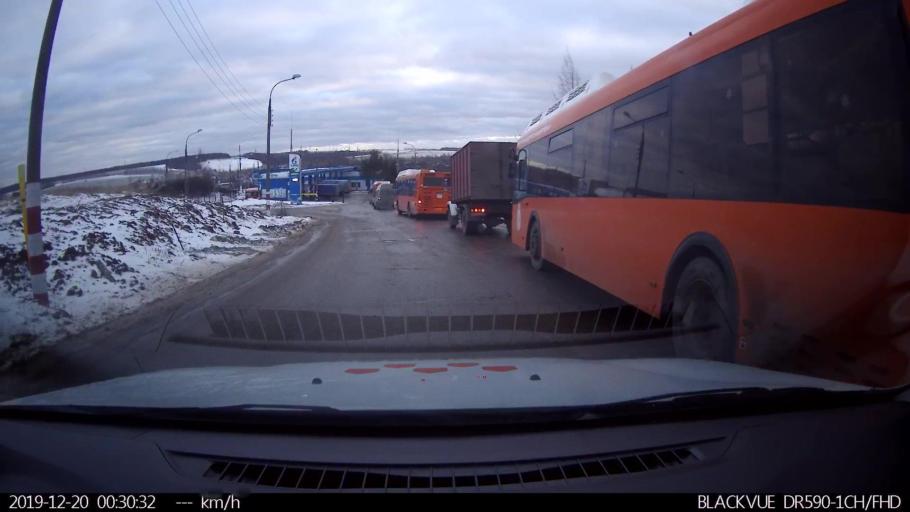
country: RU
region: Vladimir
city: Yur'yev-Pol'skiy
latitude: 56.5224
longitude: 39.6456
